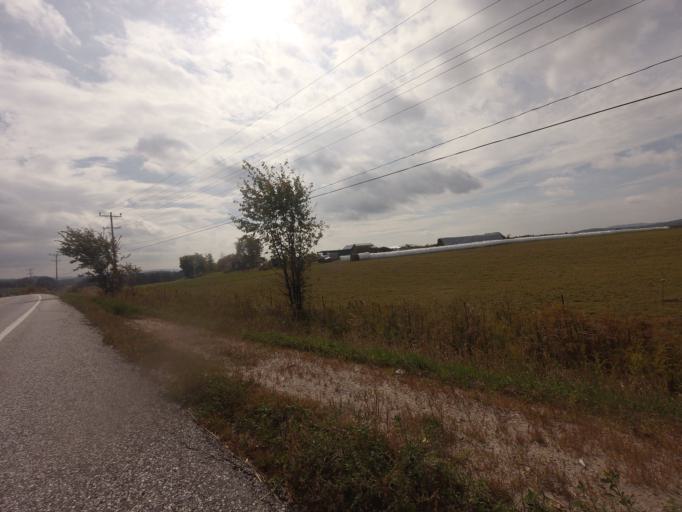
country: CA
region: Quebec
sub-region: Outaouais
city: Wakefield
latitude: 45.8559
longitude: -76.0046
